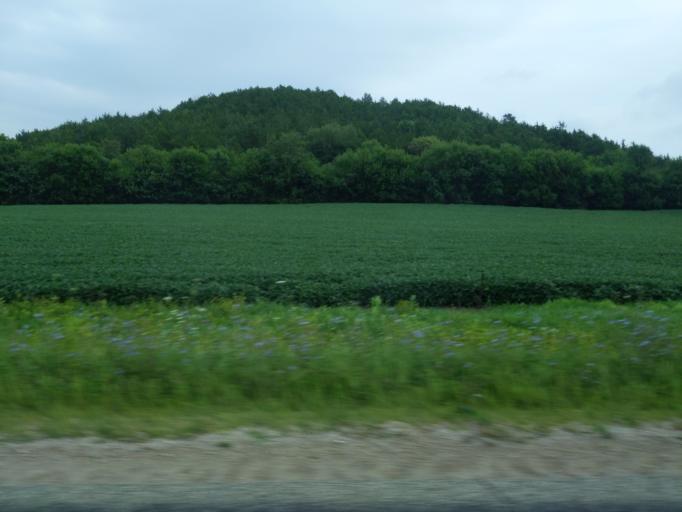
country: US
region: Wisconsin
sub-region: Dane County
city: Mazomanie
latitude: 43.1798
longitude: -89.7605
